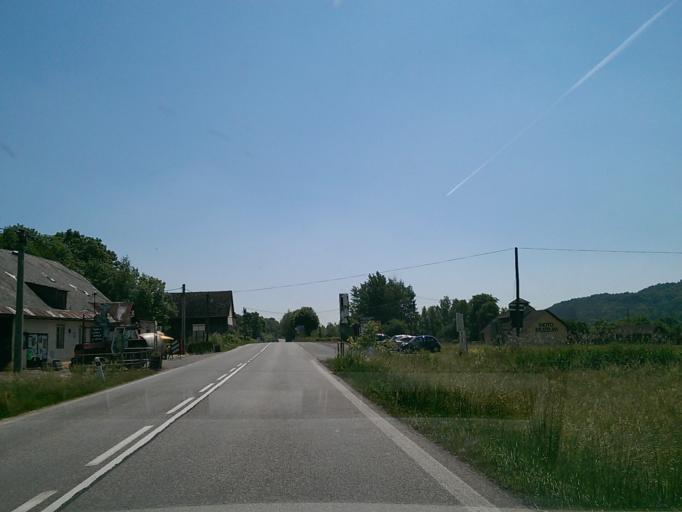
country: CZ
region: Liberecky
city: Rovensko pod Troskami
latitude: 50.5376
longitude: 15.2303
